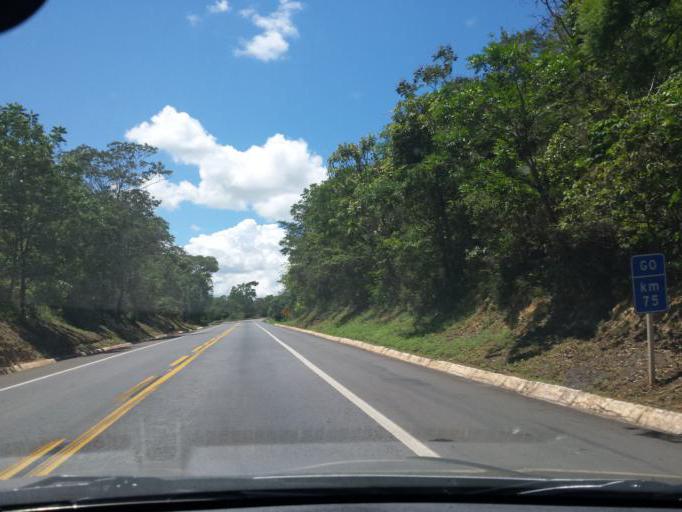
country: BR
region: Goias
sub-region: Cristalina
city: Cristalina
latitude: -16.6353
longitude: -47.7385
